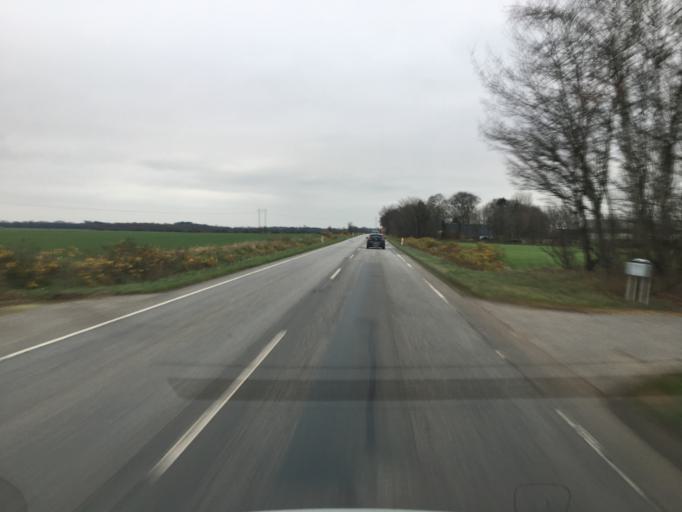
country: DK
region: South Denmark
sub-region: Aabenraa Kommune
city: Tinglev
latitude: 54.9824
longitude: 9.1652
